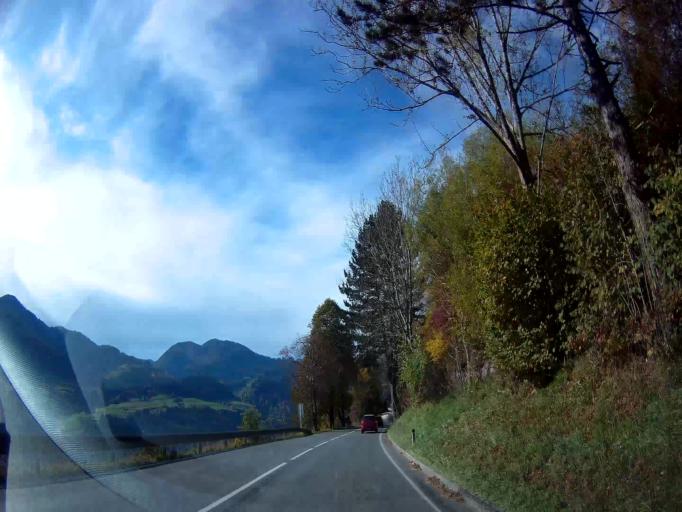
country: AT
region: Styria
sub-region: Politischer Bezirk Liezen
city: Grobming
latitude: 47.4382
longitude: 13.9010
